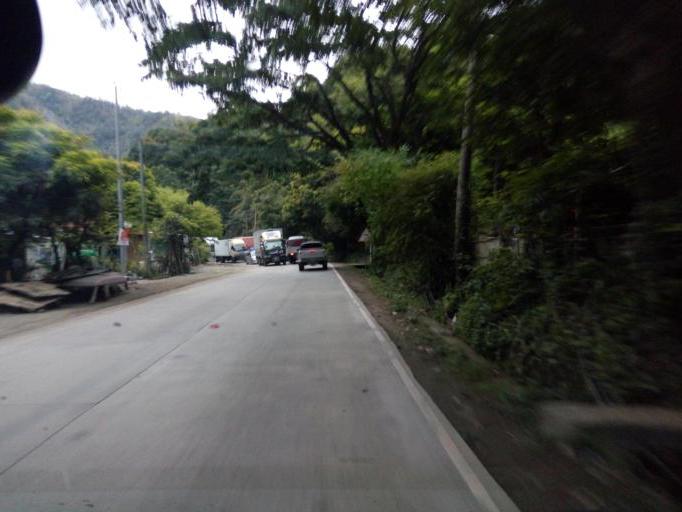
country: PH
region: Cagayan Valley
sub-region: Province of Nueva Vizcaya
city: Santa Fe
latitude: 16.1023
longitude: 120.9268
